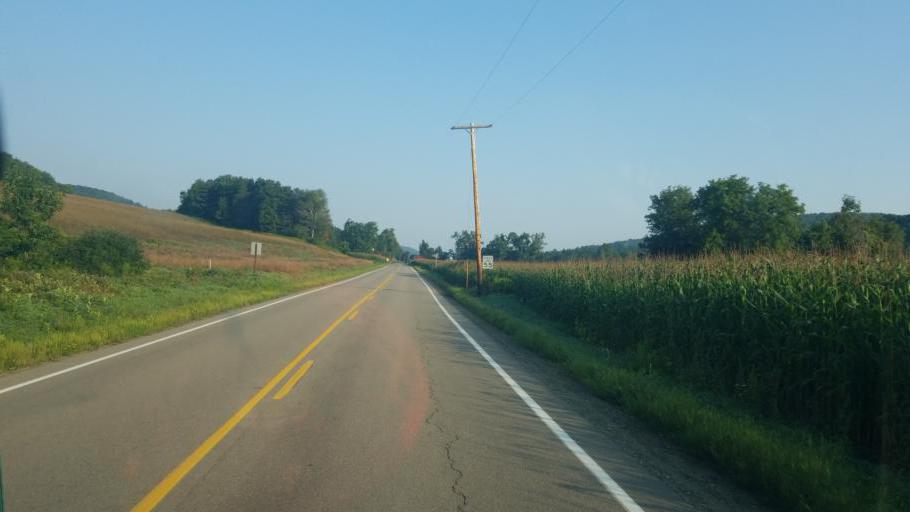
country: US
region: Pennsylvania
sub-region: Tioga County
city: Westfield
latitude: 41.9964
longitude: -77.4995
